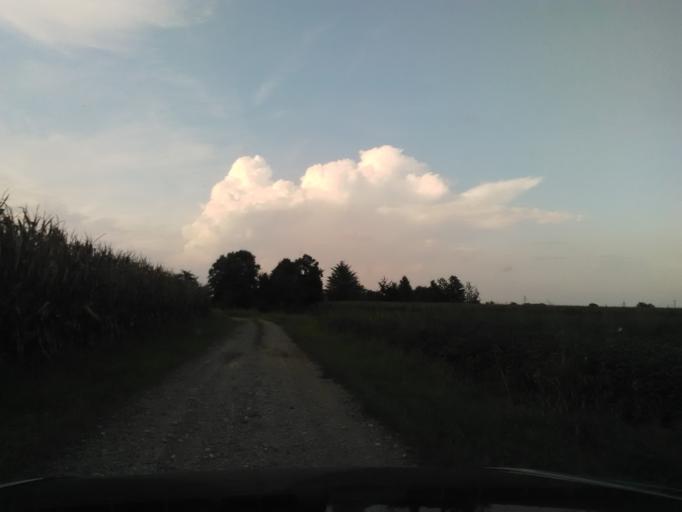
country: IT
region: Piedmont
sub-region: Provincia di Vercelli
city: Cigliano
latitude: 45.3129
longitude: 8.0446
